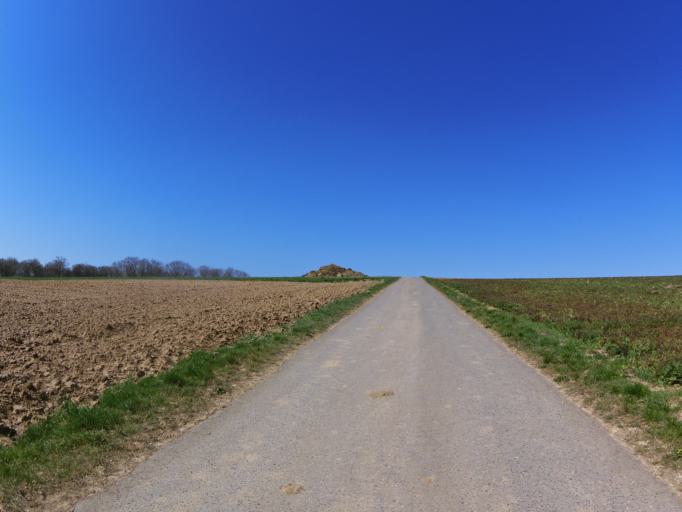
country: DE
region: Bavaria
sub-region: Regierungsbezirk Unterfranken
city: Rottendorf
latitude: 49.8115
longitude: 10.0696
